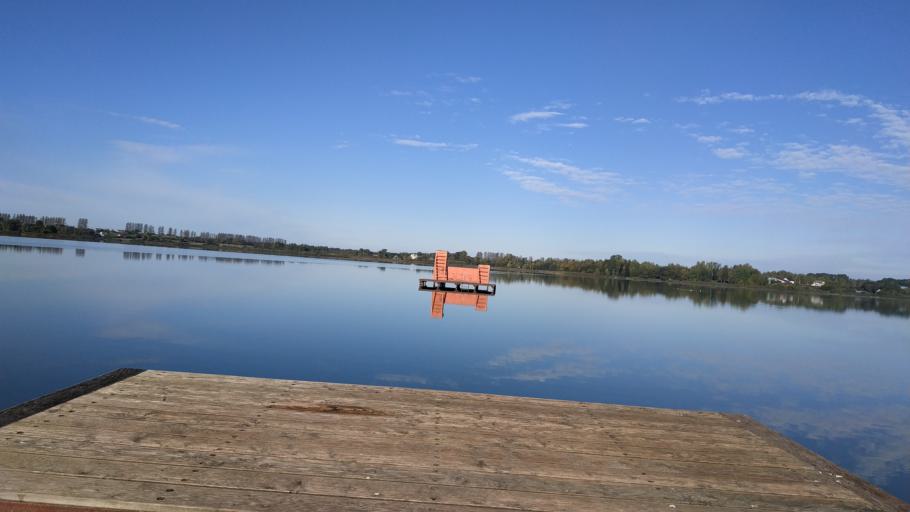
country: BY
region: Vitebsk
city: Vitebsk
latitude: 55.0893
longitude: 30.1644
